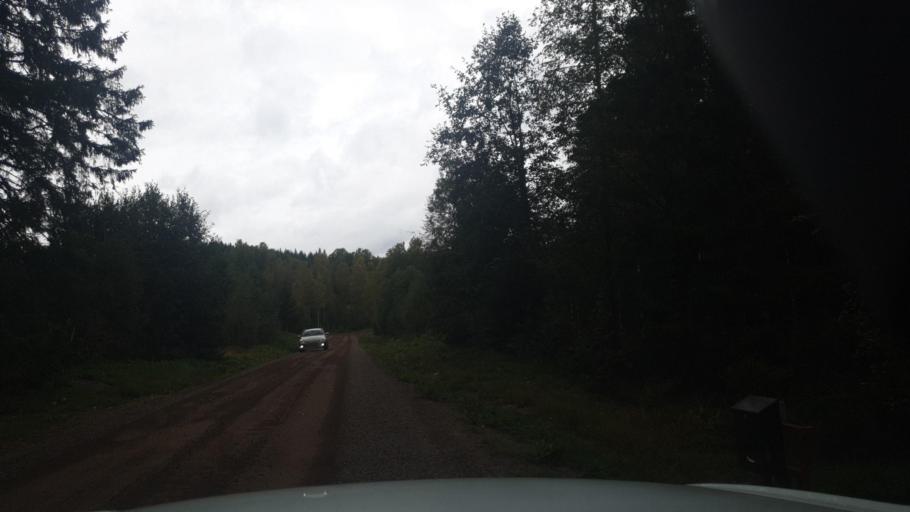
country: SE
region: Vaermland
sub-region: Arvika Kommun
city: Arvika
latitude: 59.9962
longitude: 12.6603
